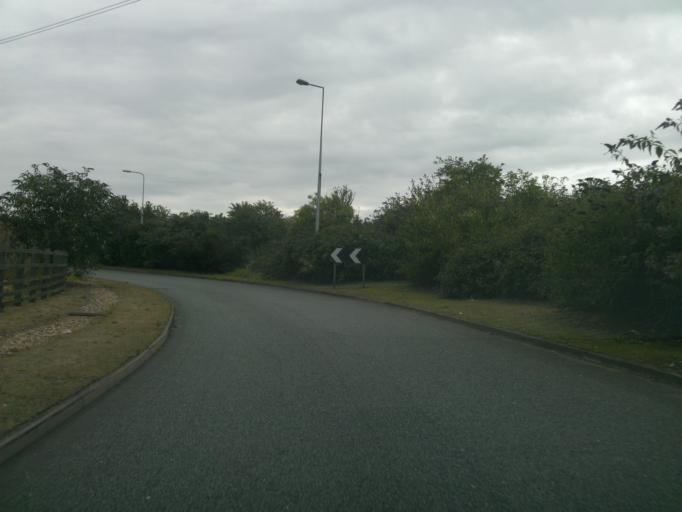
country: GB
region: England
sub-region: Kent
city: West Thurrock
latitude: 51.4893
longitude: 0.2689
